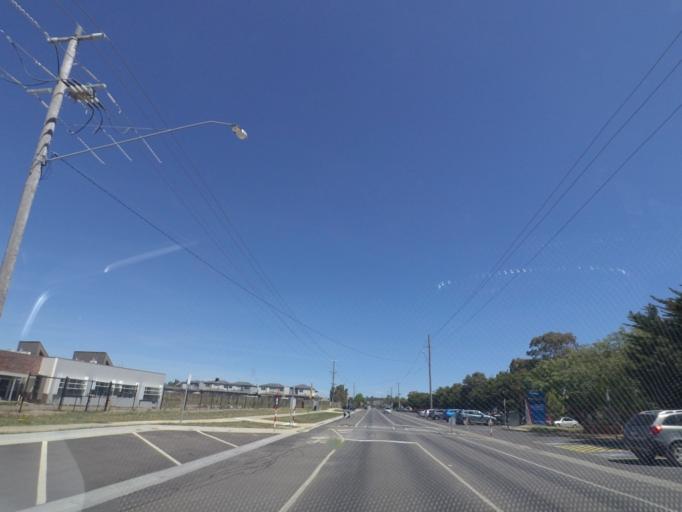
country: AU
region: Victoria
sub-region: Hume
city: Sunbury
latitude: -37.5844
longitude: 144.7056
